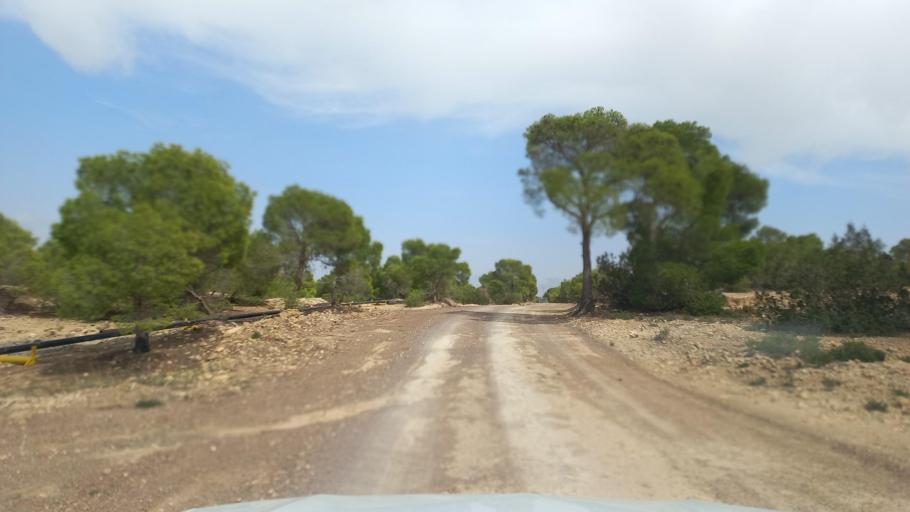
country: TN
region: Al Qasrayn
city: Kasserine
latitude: 35.3823
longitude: 8.8949
